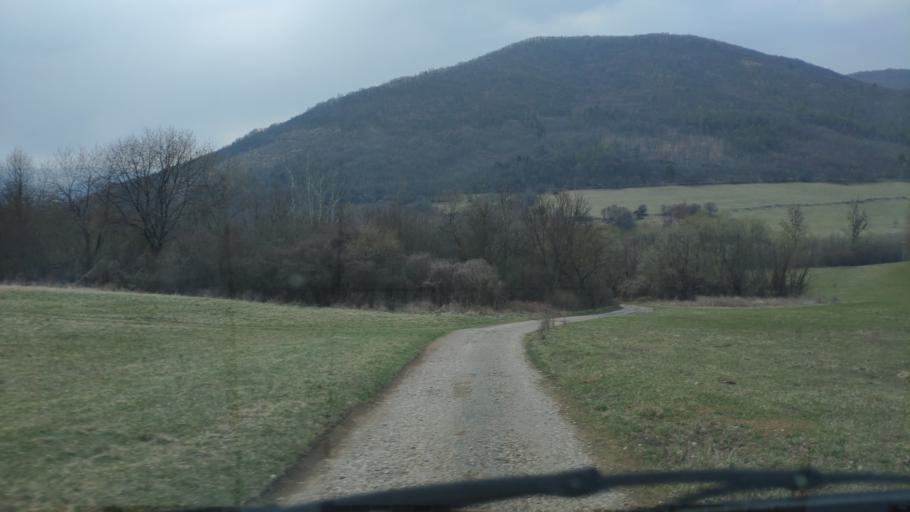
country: SK
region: Kosicky
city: Roznava
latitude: 48.6570
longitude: 20.3878
